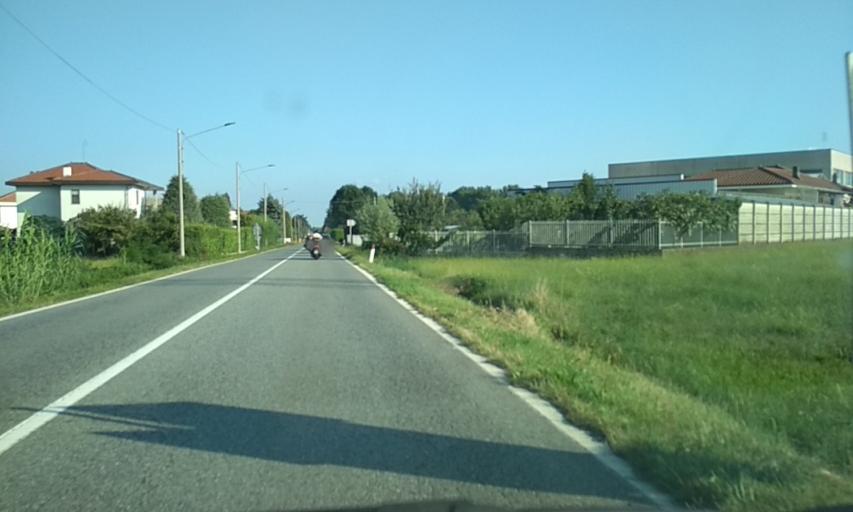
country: IT
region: Piedmont
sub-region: Provincia di Torino
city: Oglianico
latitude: 45.3466
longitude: 7.7060
